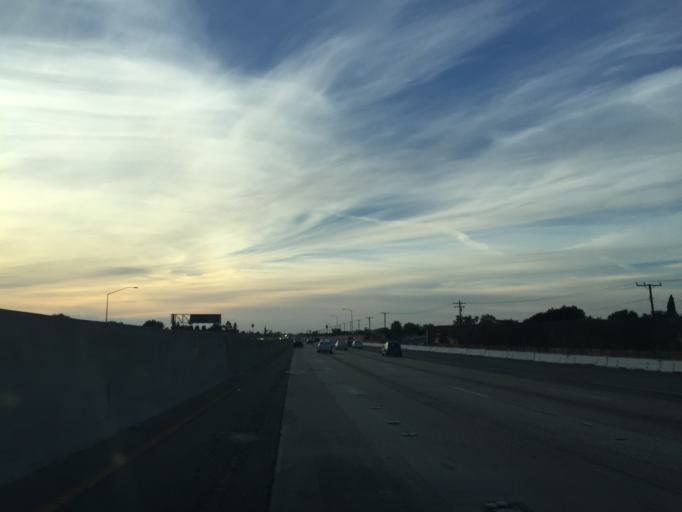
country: US
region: California
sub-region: Orange County
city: Fullerton
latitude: 33.8542
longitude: -117.9444
